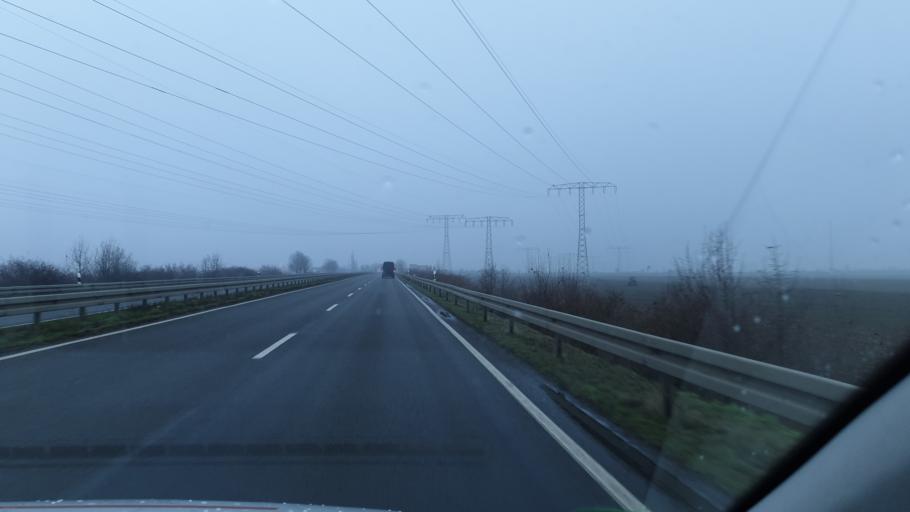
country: DE
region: Saxony
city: Markranstadt
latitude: 51.2698
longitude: 12.2658
